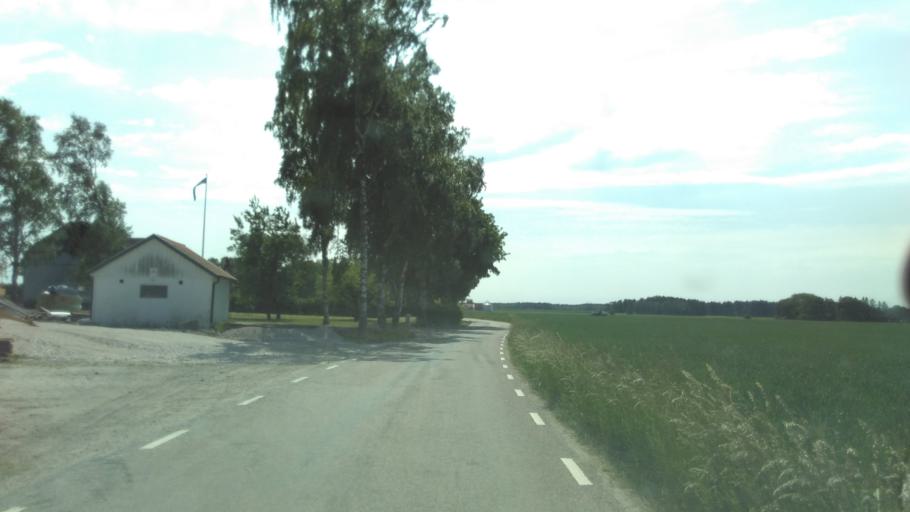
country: SE
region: Vaestra Goetaland
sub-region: Grastorps Kommun
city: Graestorp
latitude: 58.3936
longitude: 12.7932
